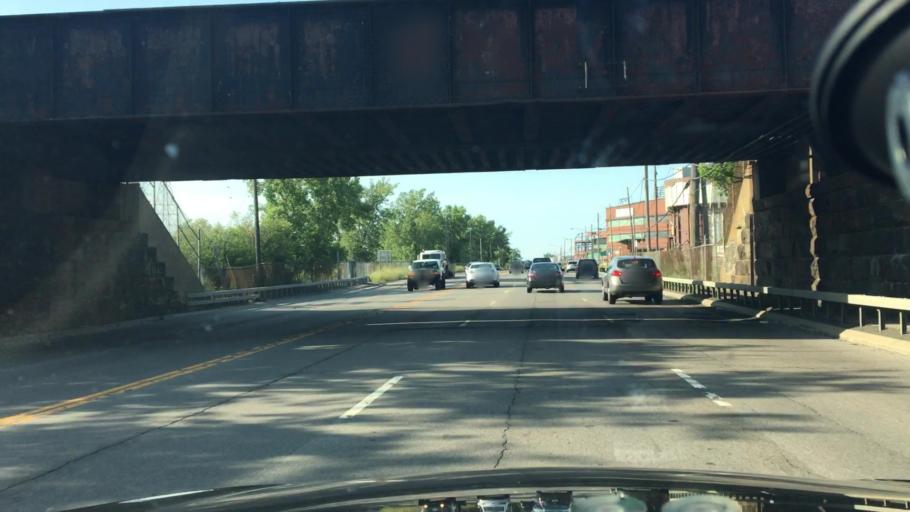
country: US
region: New York
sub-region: Erie County
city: Blasdell
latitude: 42.8039
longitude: -78.8463
